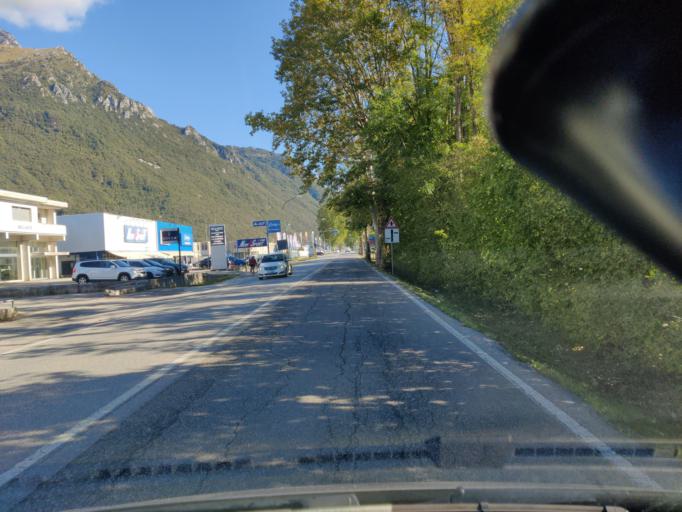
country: IT
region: Veneto
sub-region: Provincia di Belluno
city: Belluno
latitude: 46.1623
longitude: 12.2409
